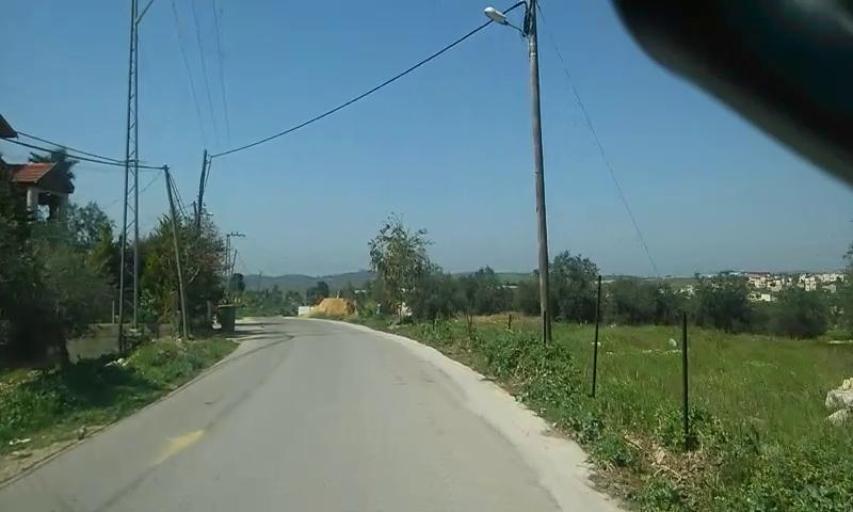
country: PS
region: West Bank
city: Al Majd
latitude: 31.4839
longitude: 34.9456
